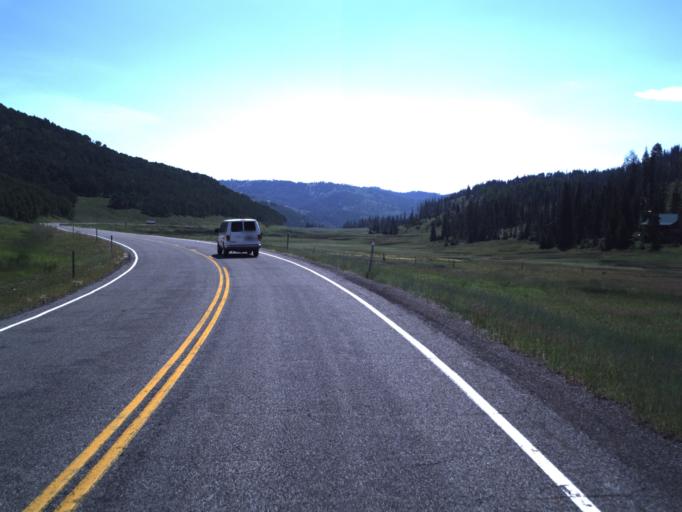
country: US
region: Utah
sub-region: Sanpete County
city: Fairview
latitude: 39.6512
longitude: -111.2868
